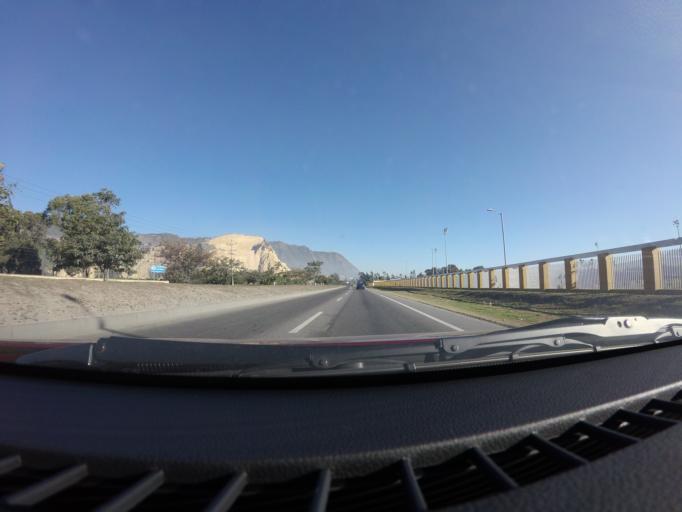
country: CO
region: Cundinamarca
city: Cajica
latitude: 4.9470
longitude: -74.0149
